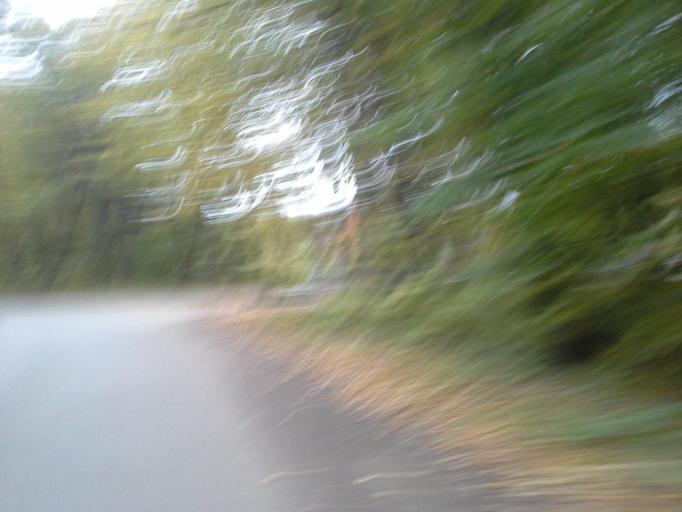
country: RU
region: Moskovskaya
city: Kokoshkino
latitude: 55.6176
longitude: 37.1448
